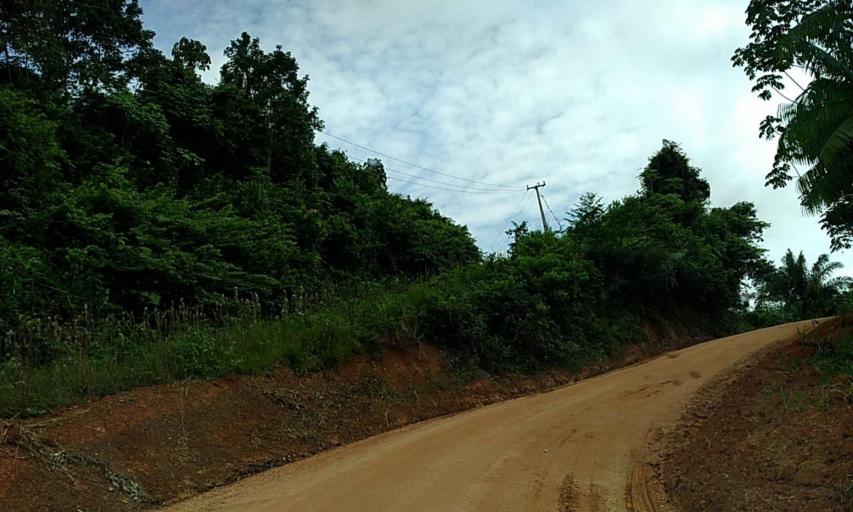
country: BR
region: Para
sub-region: Senador Jose Porfirio
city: Senador Jose Porfirio
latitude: -3.0761
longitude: -51.6354
